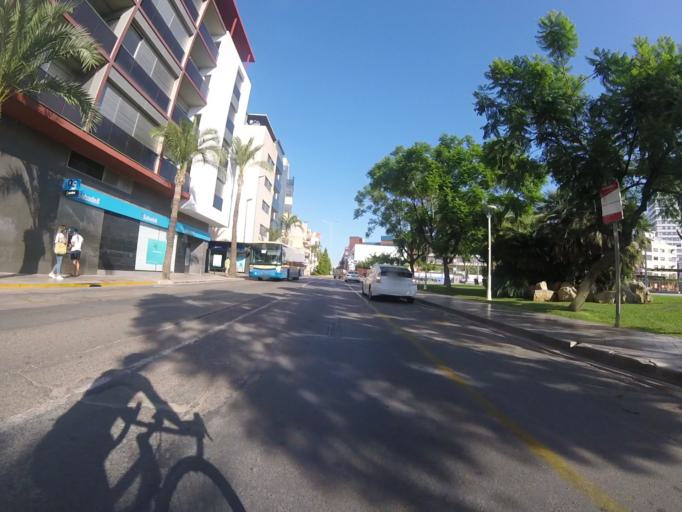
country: ES
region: Valencia
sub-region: Provincia de Castello
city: Benicarlo
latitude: 40.4161
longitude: 0.4239
